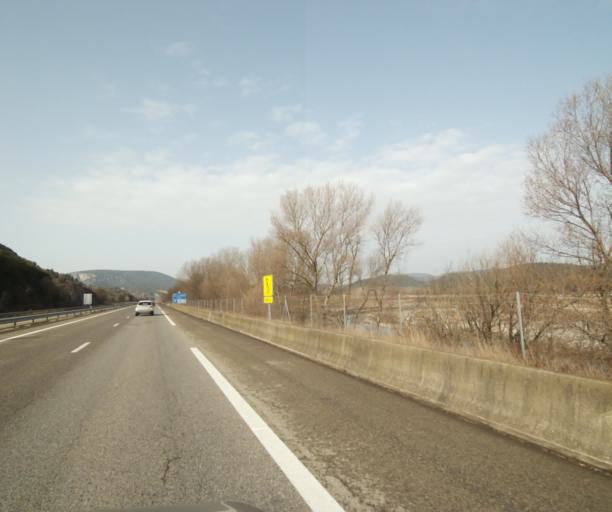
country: FR
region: Provence-Alpes-Cote d'Azur
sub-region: Departement du Vaucluse
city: Beaumont-de-Pertuis
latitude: 43.6896
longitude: 5.7003
